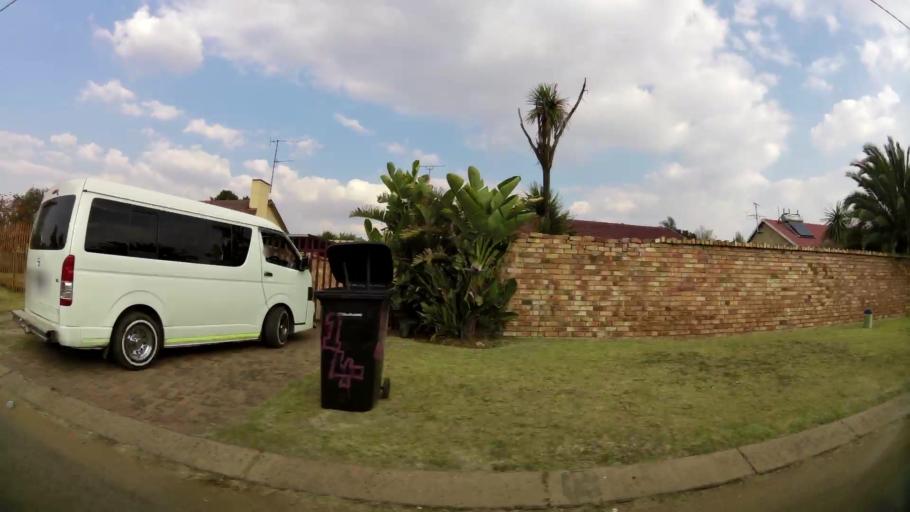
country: ZA
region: Gauteng
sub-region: City of Johannesburg Metropolitan Municipality
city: Modderfontein
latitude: -26.1116
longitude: 28.2041
